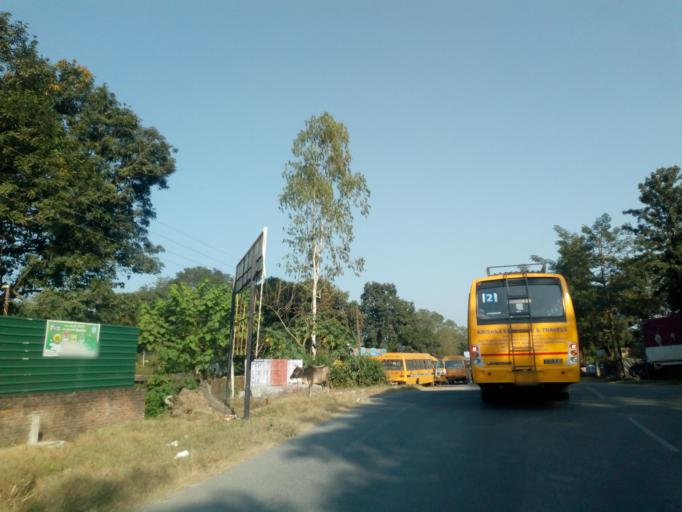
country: IN
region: Uttarakhand
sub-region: Dehradun
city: Dehradun
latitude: 30.3443
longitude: 77.9131
